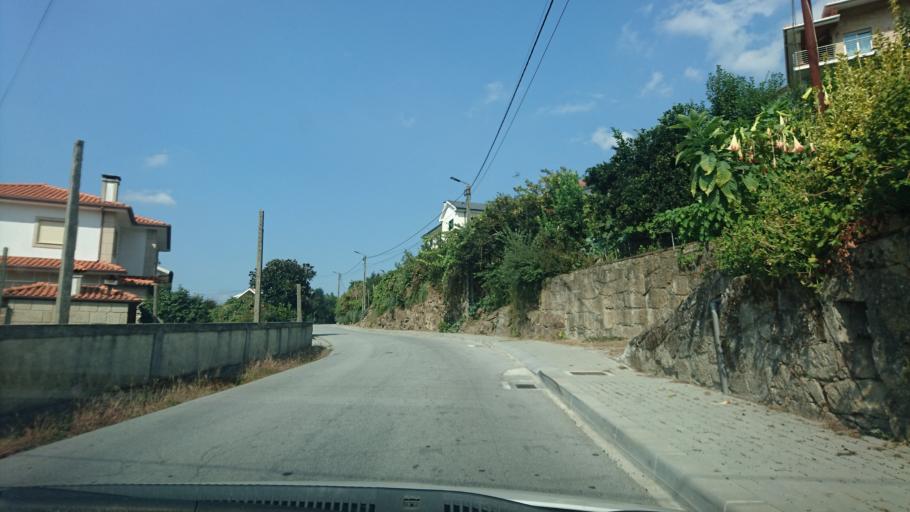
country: PT
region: Vila Real
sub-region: Mondim de Basto
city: Mondim de Basto
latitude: 41.4131
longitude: -7.9487
